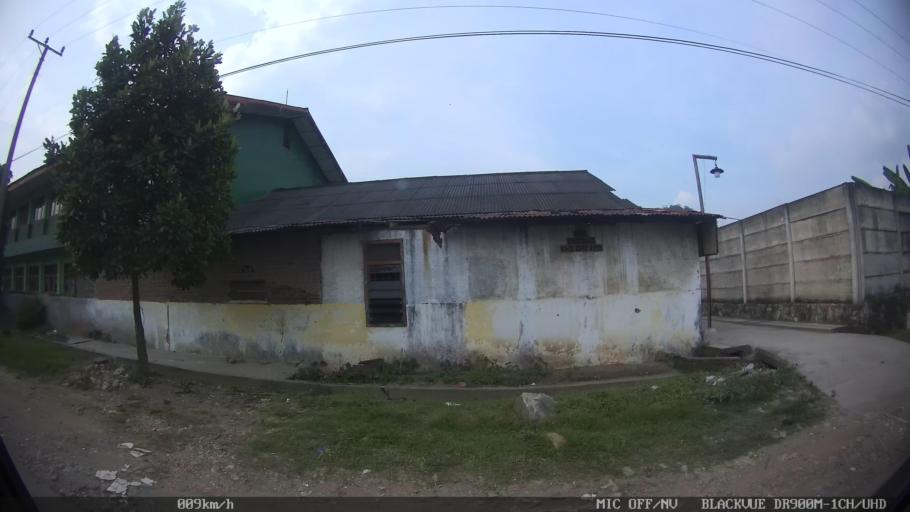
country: ID
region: Lampung
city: Panjang
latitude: -5.4458
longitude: 105.3088
